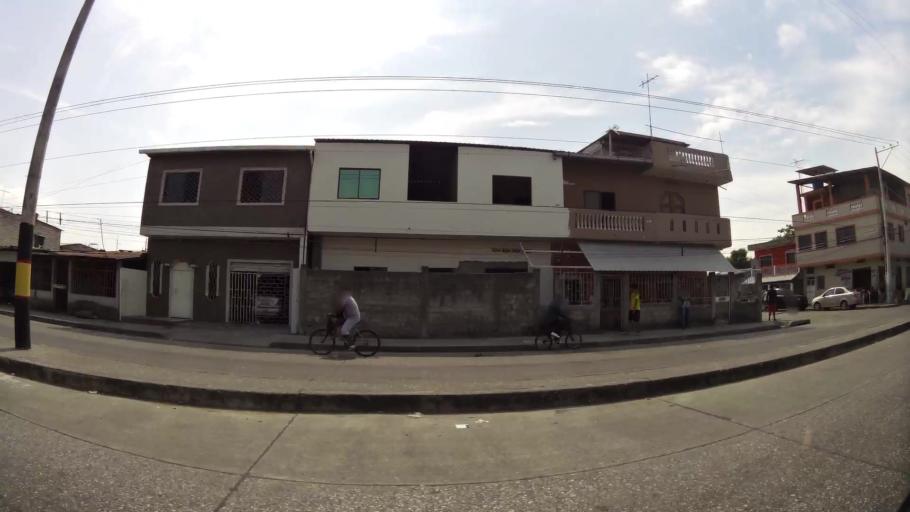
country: EC
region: Guayas
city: Guayaquil
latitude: -2.2769
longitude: -79.8857
